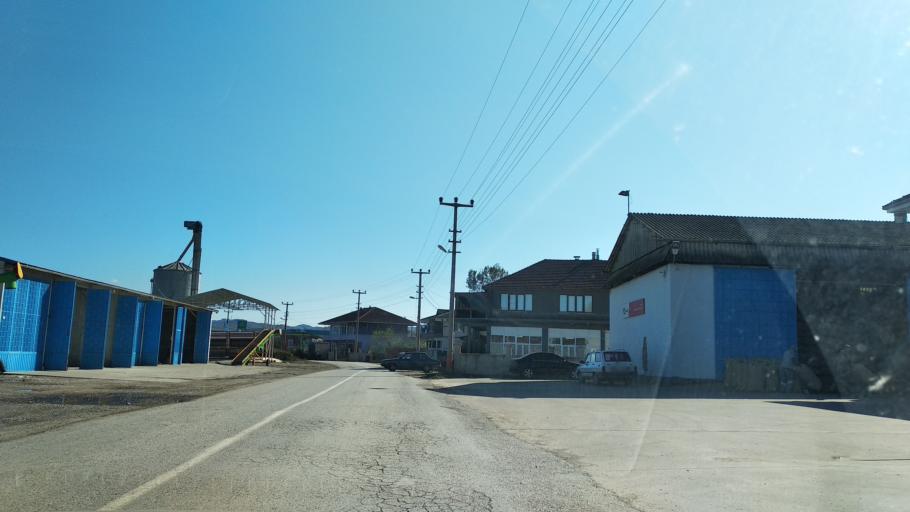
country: TR
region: Sakarya
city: Ortakoy
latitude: 41.0287
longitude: 30.5954
